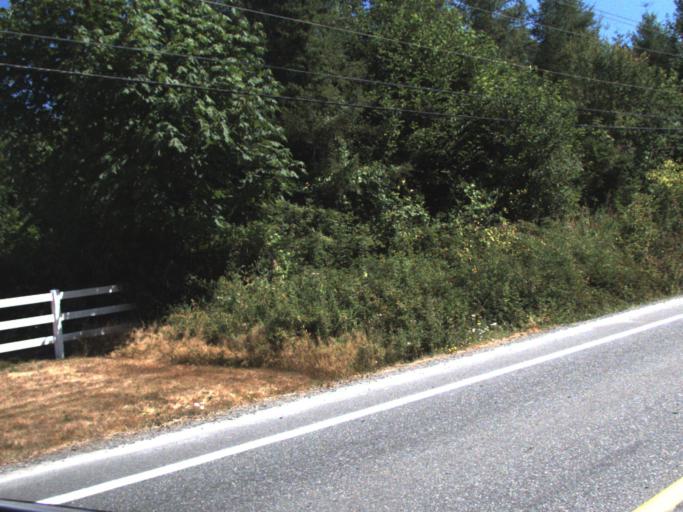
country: US
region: Washington
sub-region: King County
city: Fall City
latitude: 47.5777
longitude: -121.9276
